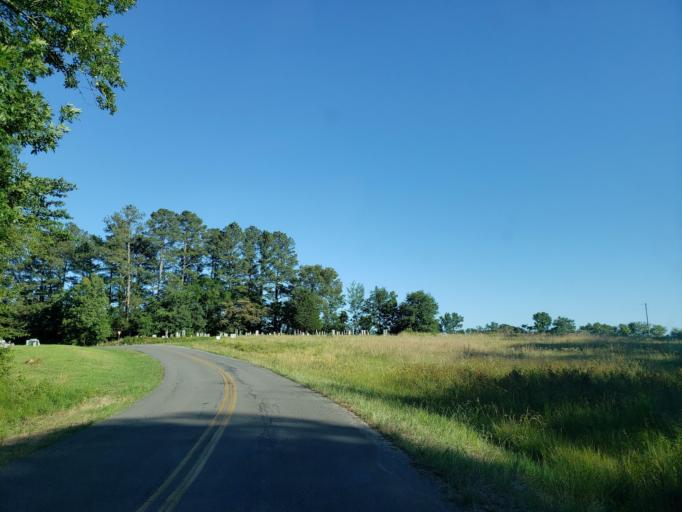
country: US
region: Georgia
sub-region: Floyd County
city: Shannon
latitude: 34.4934
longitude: -85.1142
